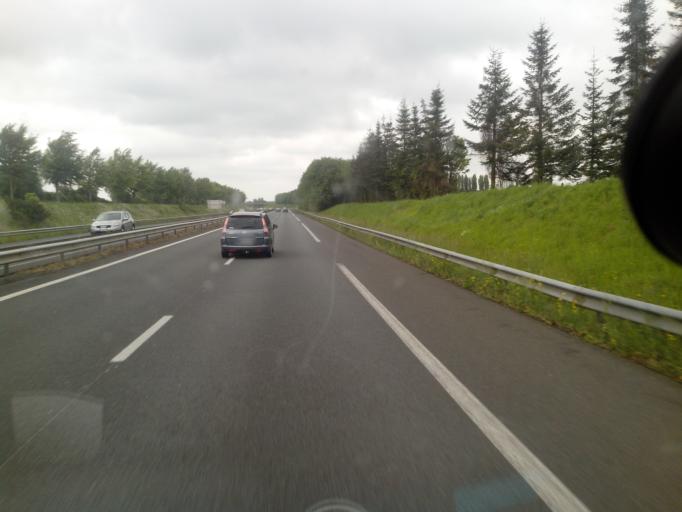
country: FR
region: Lower Normandy
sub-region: Departement du Calvados
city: Grainville-sur-Odon
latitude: 49.1435
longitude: -0.5307
